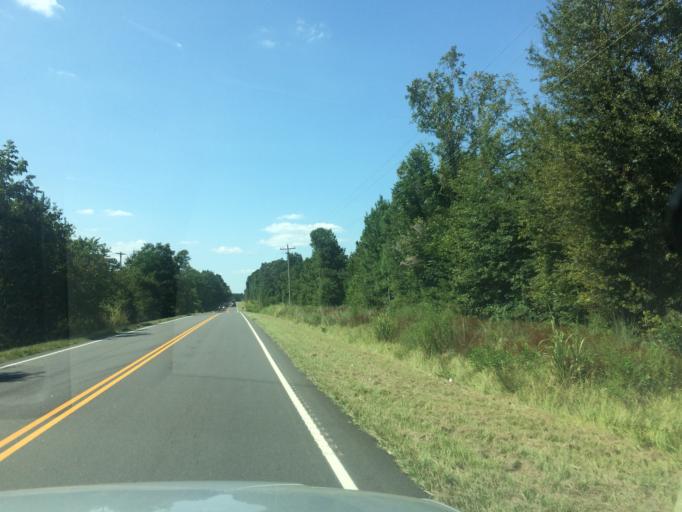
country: US
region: South Carolina
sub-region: Lexington County
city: Batesburg-Leesville
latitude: 33.7051
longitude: -81.4854
